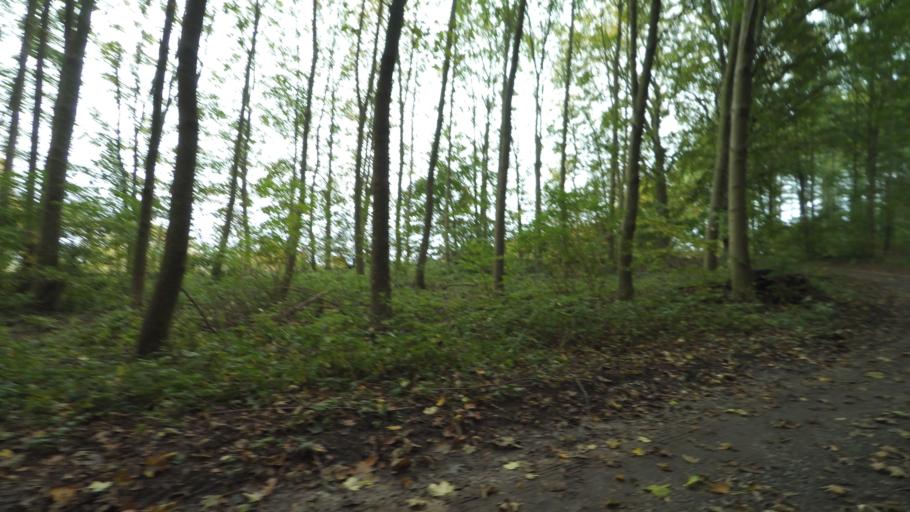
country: DK
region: Central Jutland
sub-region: Arhus Kommune
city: Stavtrup
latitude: 56.1506
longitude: 10.0982
